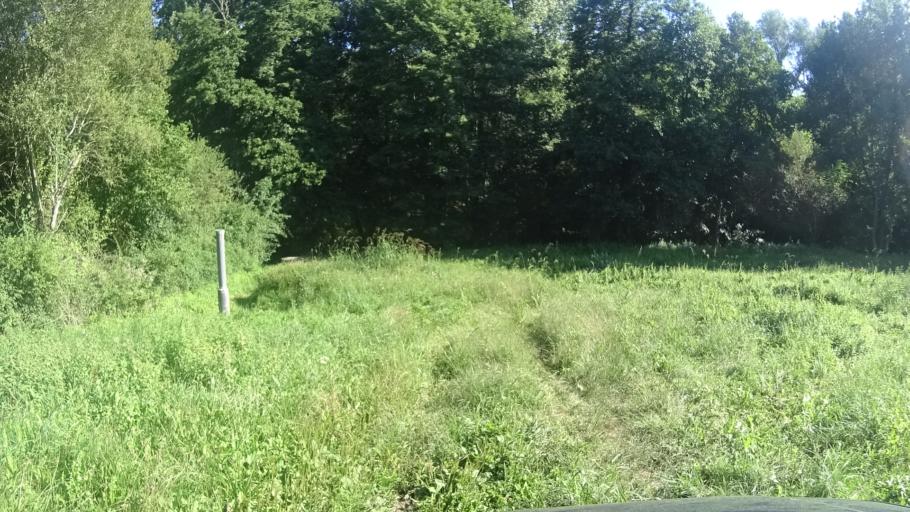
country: FR
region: Aquitaine
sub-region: Departement de la Dordogne
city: Sourzac
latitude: 45.0171
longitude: 0.4039
